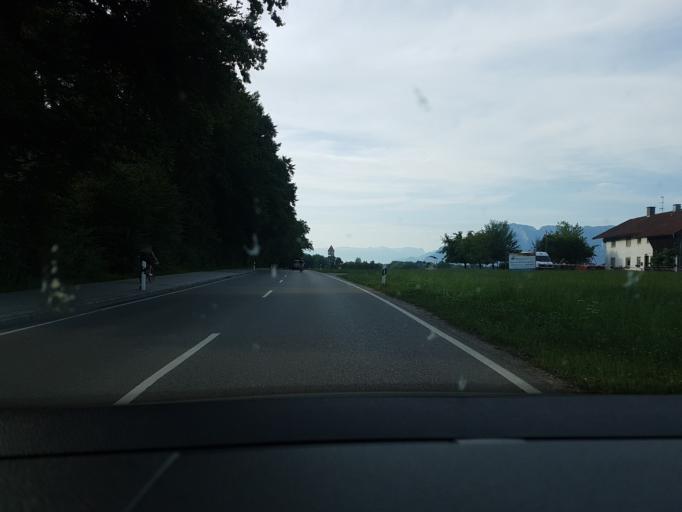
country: DE
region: Bavaria
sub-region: Upper Bavaria
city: Ainring
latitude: 47.8525
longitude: 12.9393
